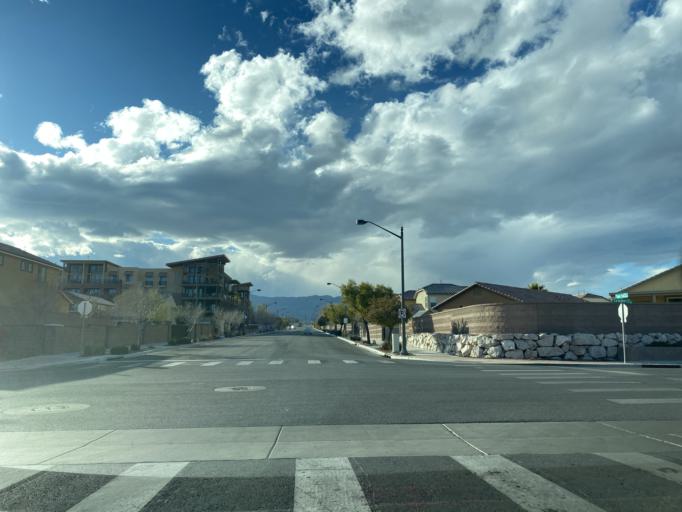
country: US
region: Nevada
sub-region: Clark County
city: Summerlin South
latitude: 36.2828
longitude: -115.2922
